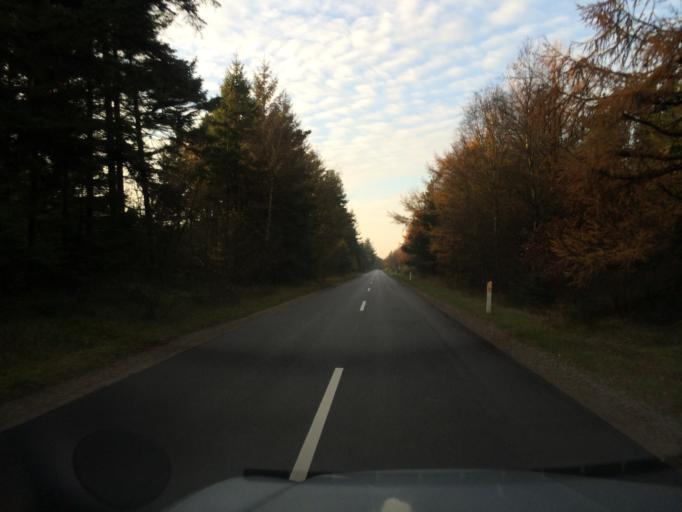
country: DK
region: Central Jutland
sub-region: Holstebro Kommune
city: Ulfborg
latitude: 56.2586
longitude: 8.3505
